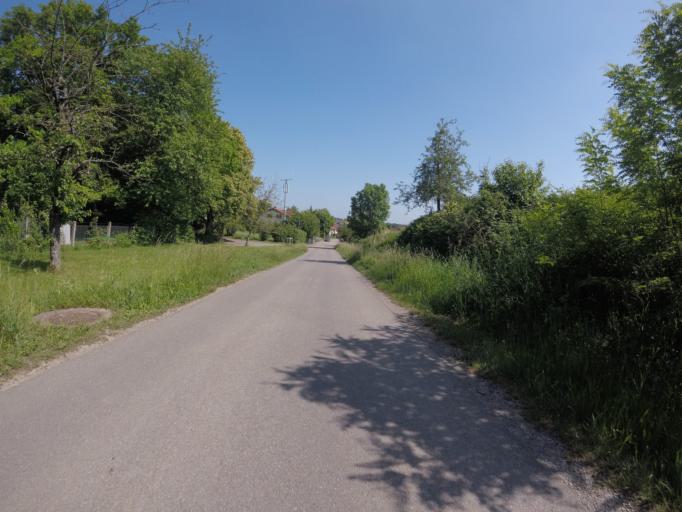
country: DE
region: Baden-Wuerttemberg
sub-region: Regierungsbezirk Stuttgart
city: Kirchberg an der Murr
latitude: 48.9660
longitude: 9.3272
